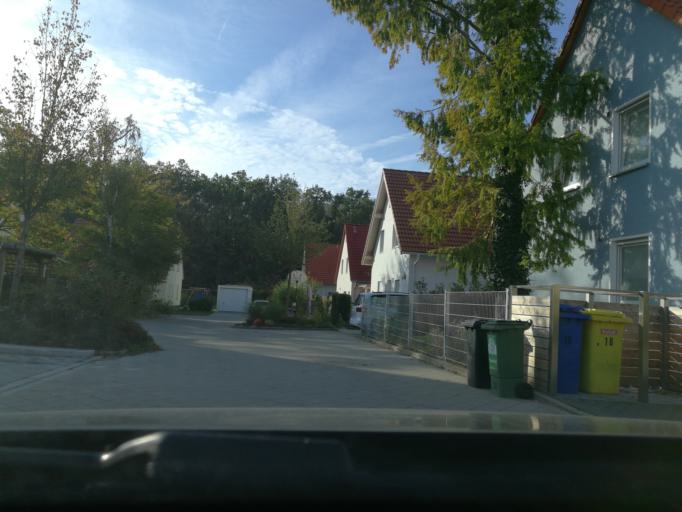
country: DE
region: Bavaria
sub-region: Regierungsbezirk Mittelfranken
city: Seukendorf
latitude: 49.4891
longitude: 10.9065
